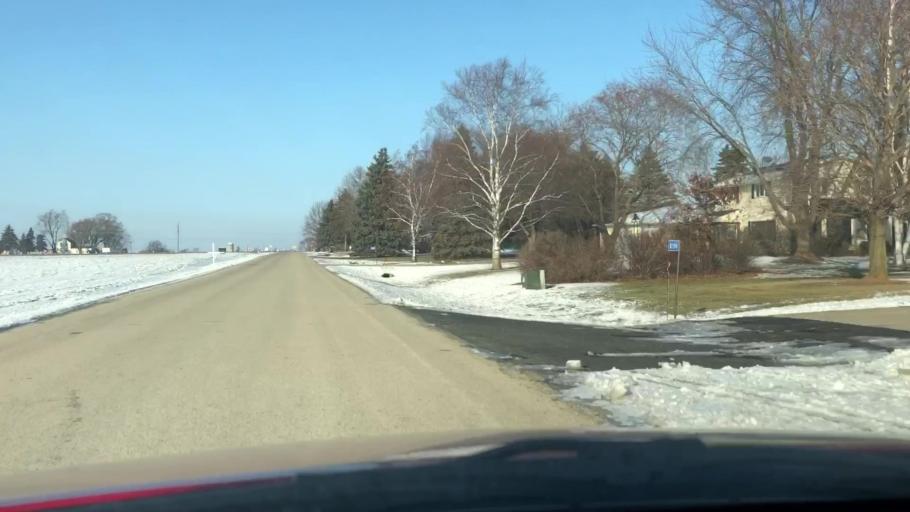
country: US
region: Wisconsin
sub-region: Outagamie County
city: Seymour
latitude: 44.4975
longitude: -88.3089
